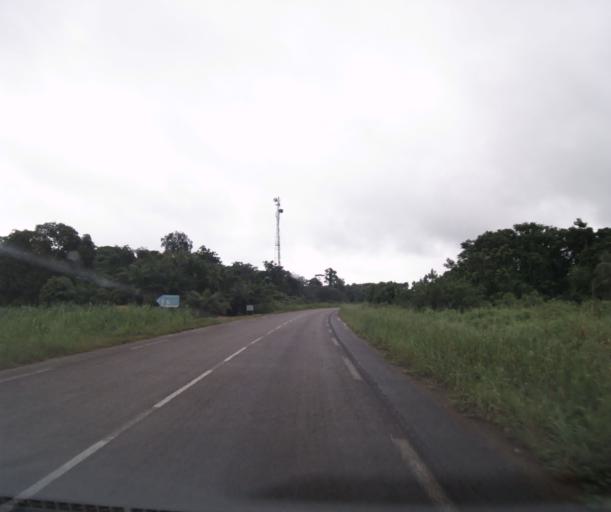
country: CM
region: Littoral
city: Dizangue
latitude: 3.5072
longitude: 10.1178
